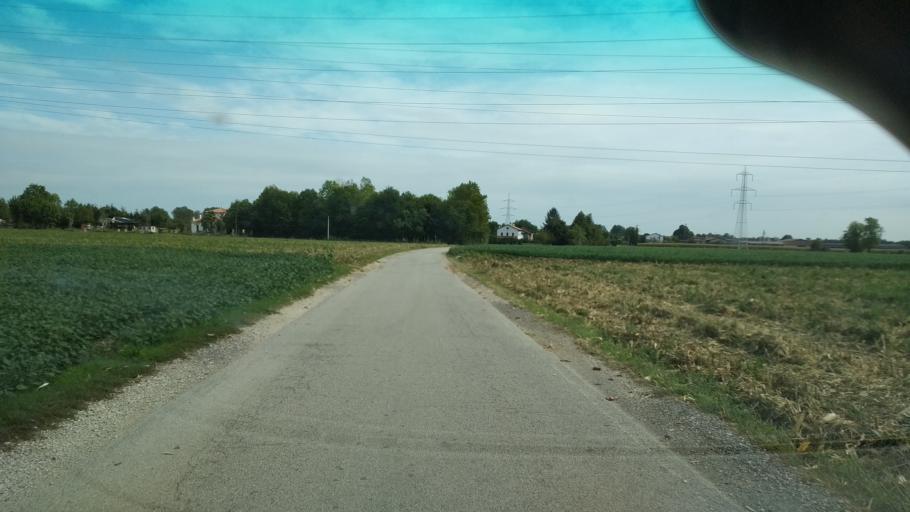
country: IT
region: Veneto
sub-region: Provincia di Vicenza
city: Sandrigo
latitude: 45.6418
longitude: 11.5838
